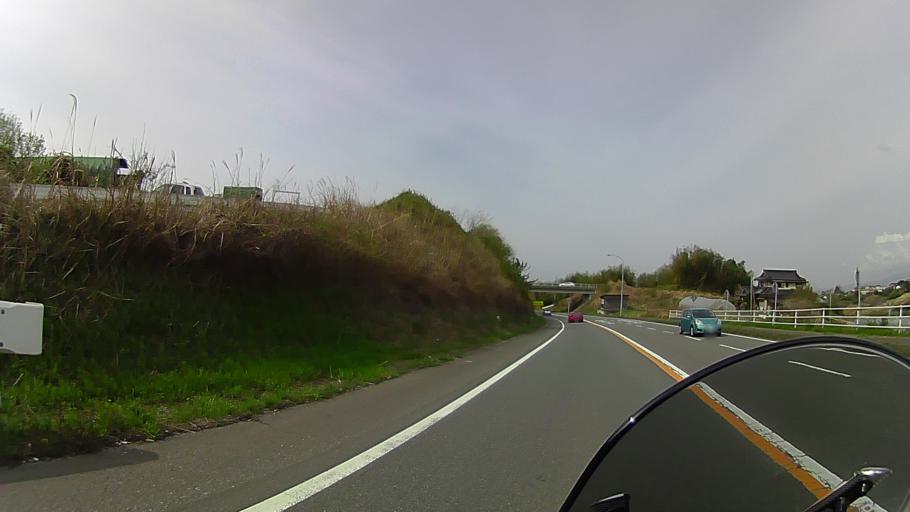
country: JP
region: Shizuoka
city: Mishima
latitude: 35.1370
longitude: 138.9685
